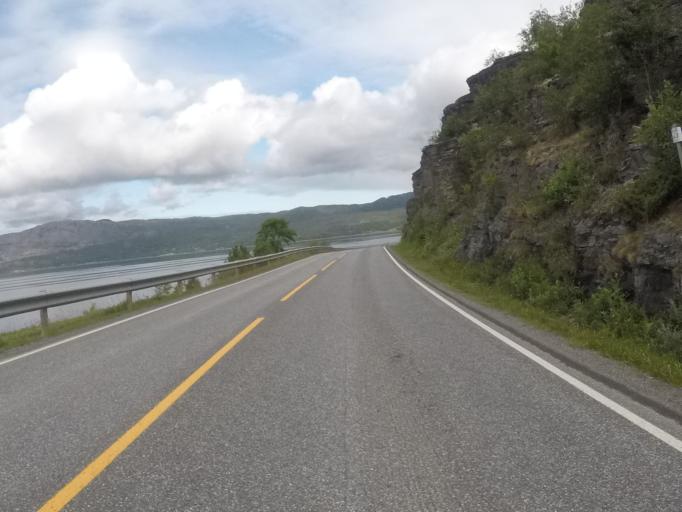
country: NO
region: Finnmark Fylke
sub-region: Alta
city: Alta
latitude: 69.9980
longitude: 23.4790
